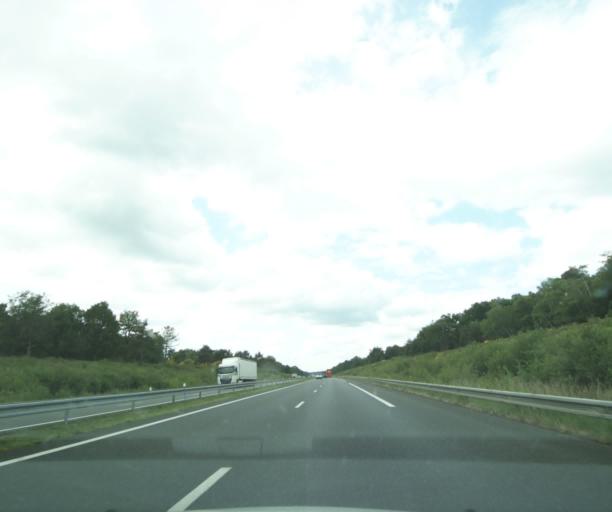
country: FR
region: Centre
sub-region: Departement du Loir-et-Cher
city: Lamotte-Beuvron
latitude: 47.5706
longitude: 2.0036
